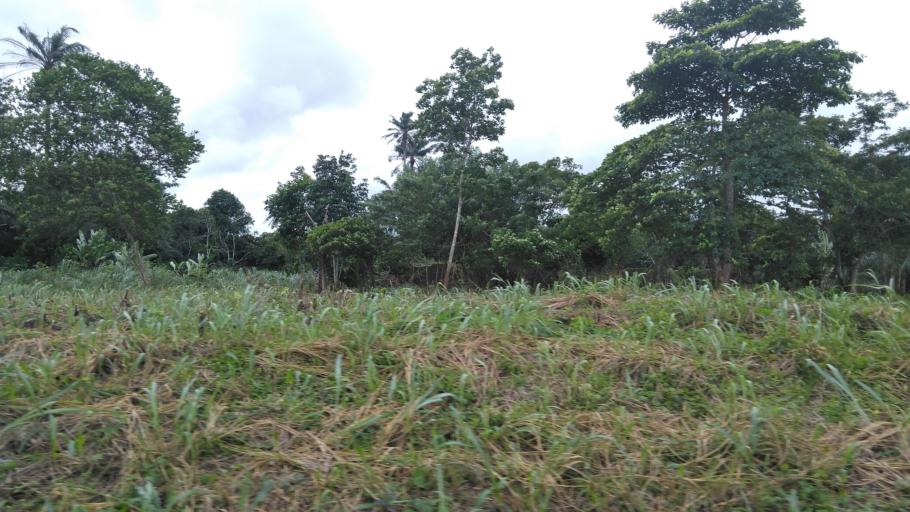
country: NG
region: Ogun
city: Abigi
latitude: 6.5934
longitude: 4.4983
